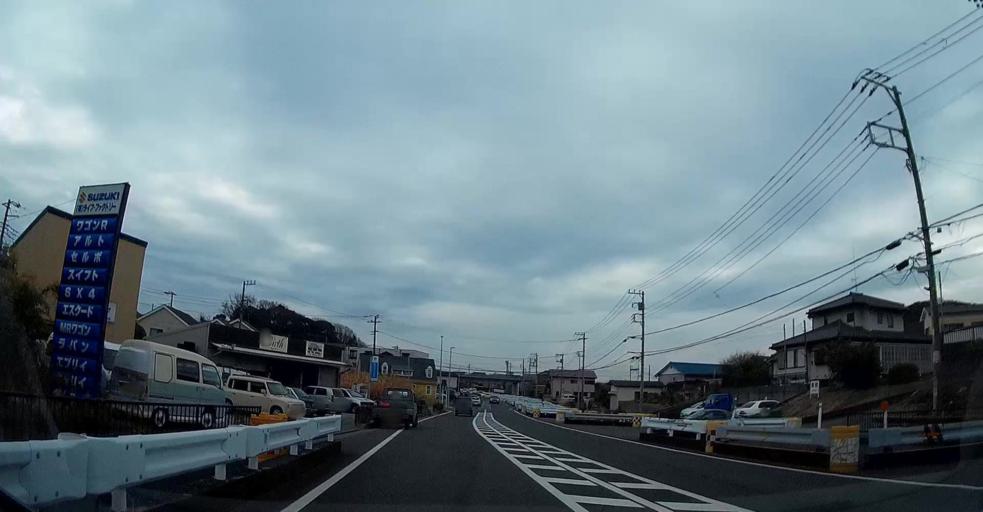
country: JP
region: Kanagawa
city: Yokosuka
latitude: 35.2089
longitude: 139.6777
